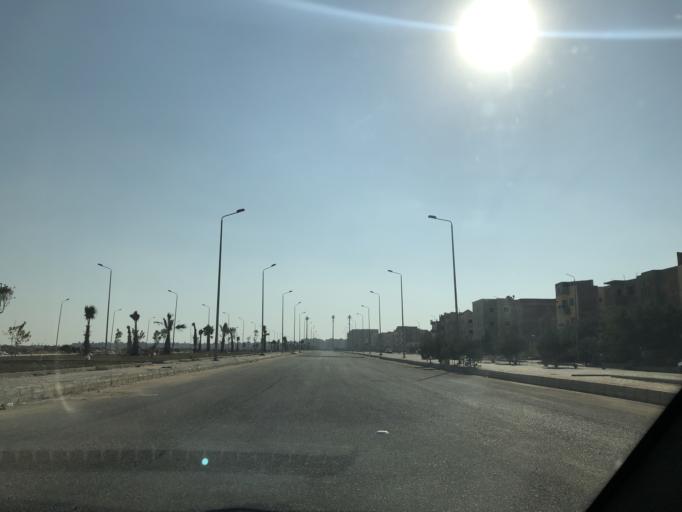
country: EG
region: Al Jizah
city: Madinat Sittah Uktubar
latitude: 29.9238
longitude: 31.0666
